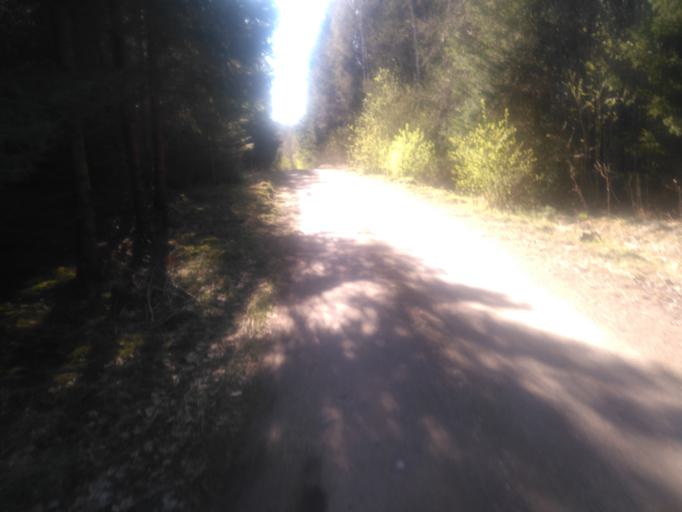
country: LV
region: Vecpiebalga
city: Vecpiebalga
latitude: 57.0066
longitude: 25.8500
